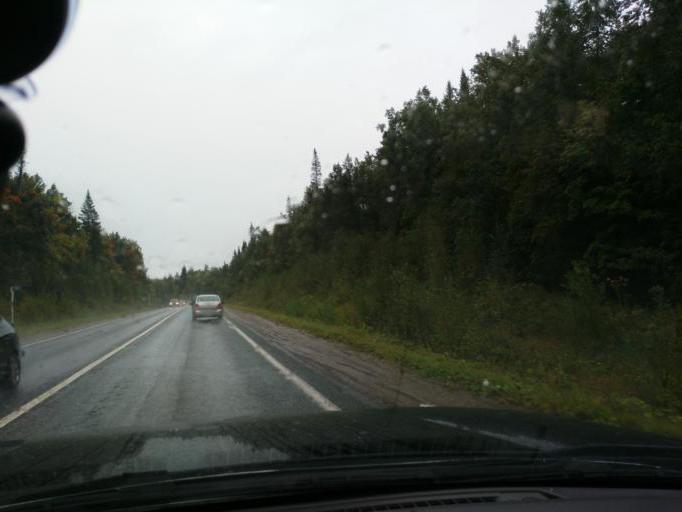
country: RU
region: Perm
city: Yugo-Kamskiy
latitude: 57.6010
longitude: 55.6540
